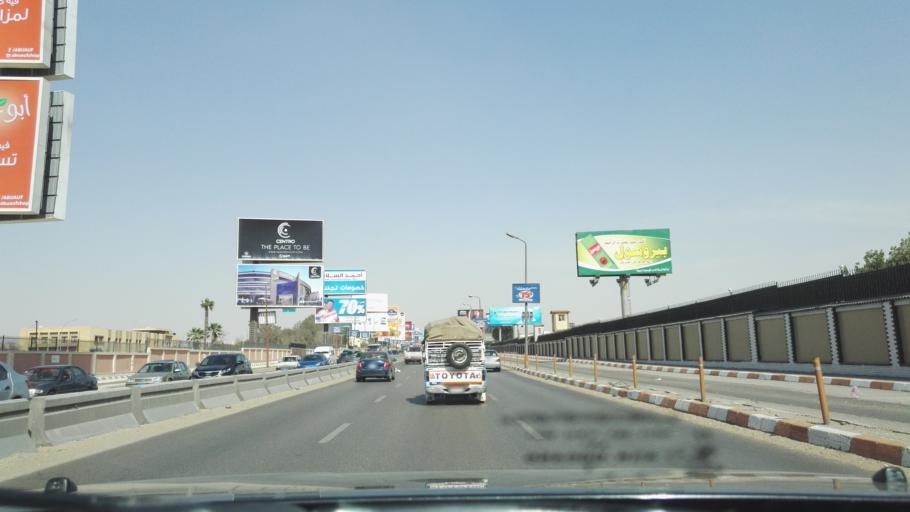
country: EG
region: Muhafazat al Qalyubiyah
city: Al Khankah
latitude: 30.0804
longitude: 31.3938
